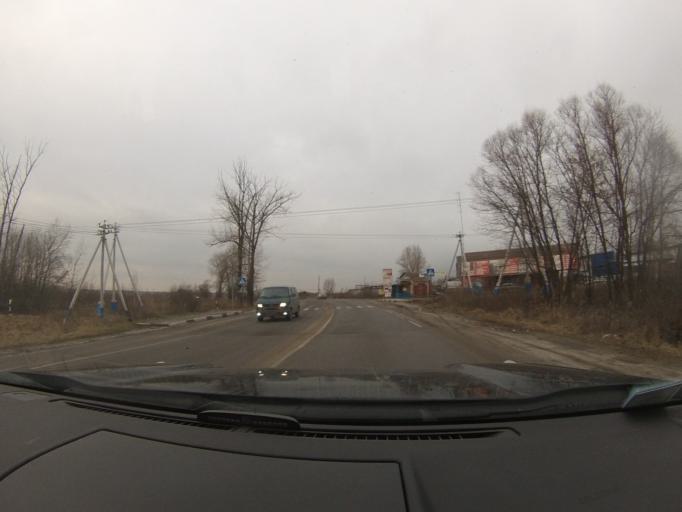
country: RU
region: Moskovskaya
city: Lopatinskiy
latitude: 55.3255
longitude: 38.7356
